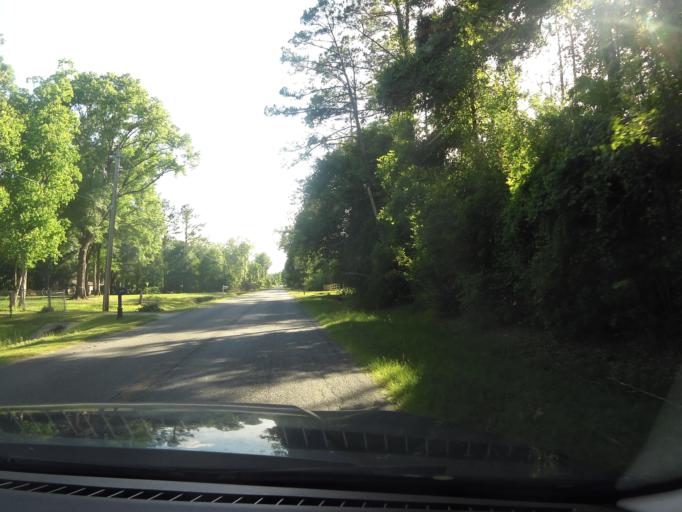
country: US
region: Florida
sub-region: Nassau County
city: Nassau Village-Ratliff
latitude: 30.4917
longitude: -81.8242
